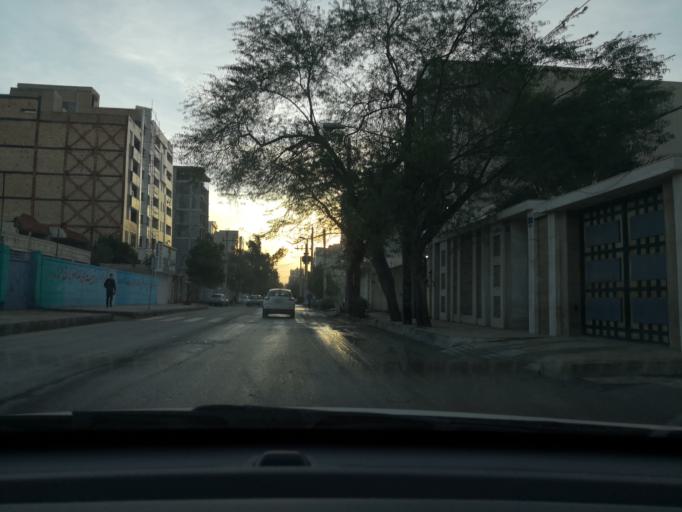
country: IR
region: Khuzestan
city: Ahvaz
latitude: 31.3513
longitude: 48.6830
